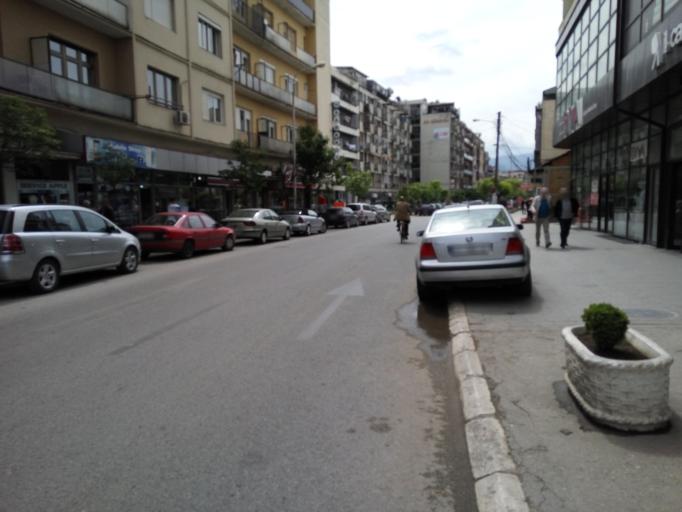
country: XK
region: Gjakova
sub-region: Komuna e Gjakoves
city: Gjakove
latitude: 42.3831
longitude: 20.4303
